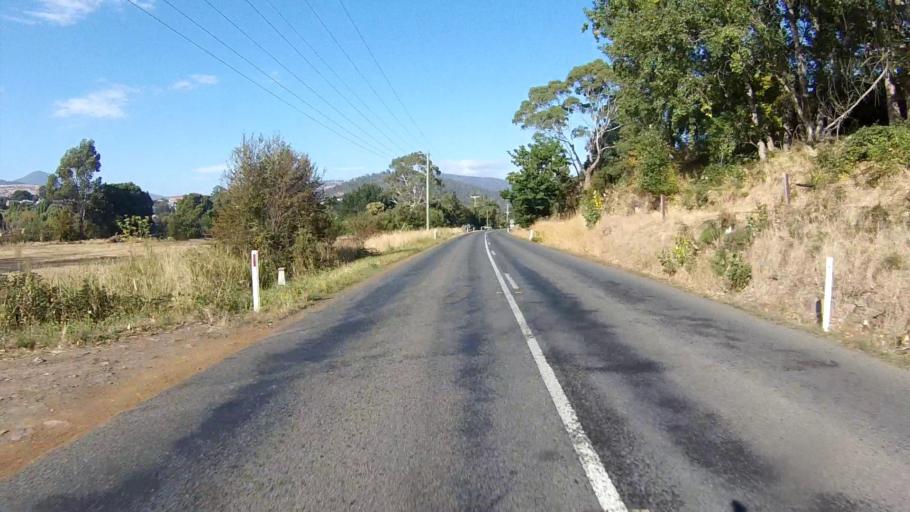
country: AU
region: Tasmania
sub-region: Derwent Valley
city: New Norfolk
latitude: -42.7726
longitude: 147.0662
